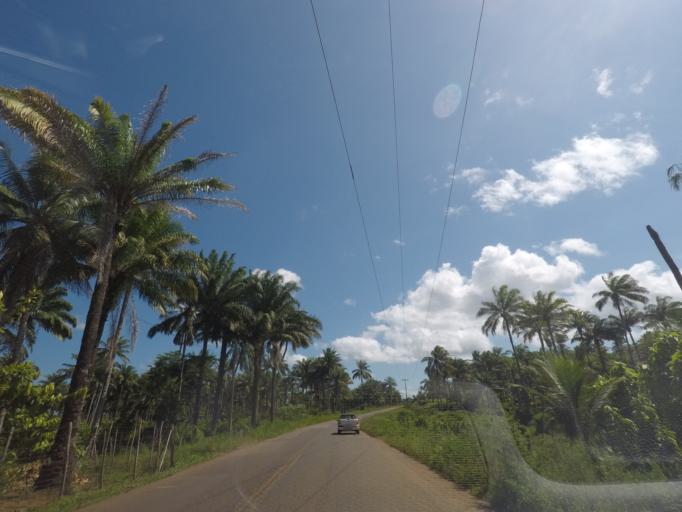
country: BR
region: Bahia
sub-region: Taperoa
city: Taperoa
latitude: -13.5614
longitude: -39.1048
